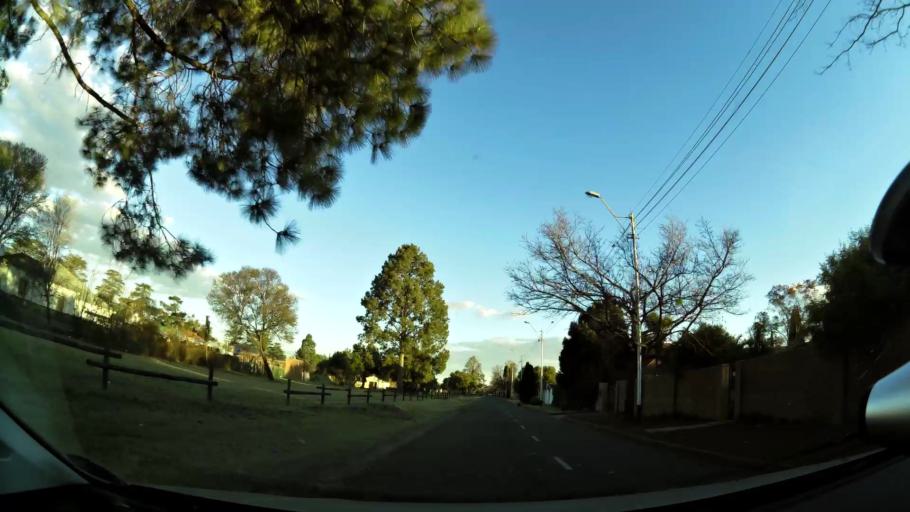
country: ZA
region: North-West
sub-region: Dr Kenneth Kaunda District Municipality
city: Potchefstroom
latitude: -26.7218
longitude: 27.0894
